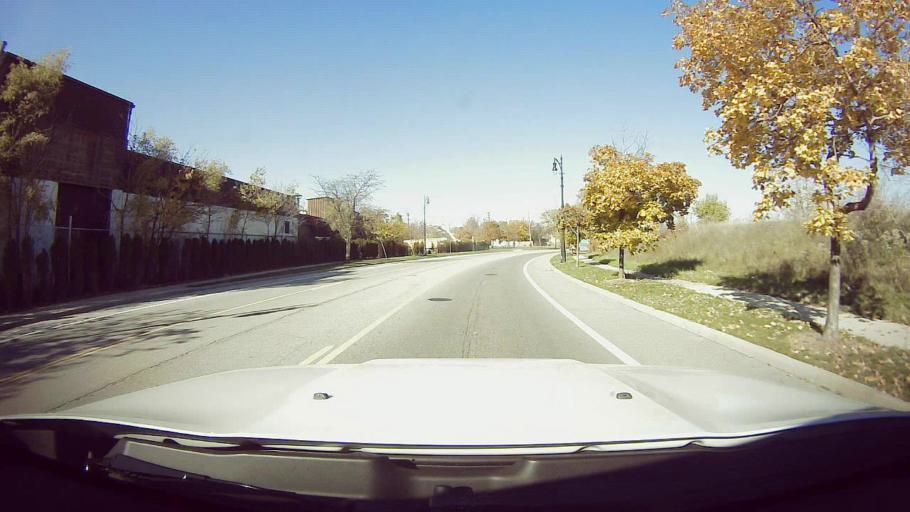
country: US
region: Michigan
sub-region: Wayne County
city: Hamtramck
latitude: 42.3606
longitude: -83.0835
